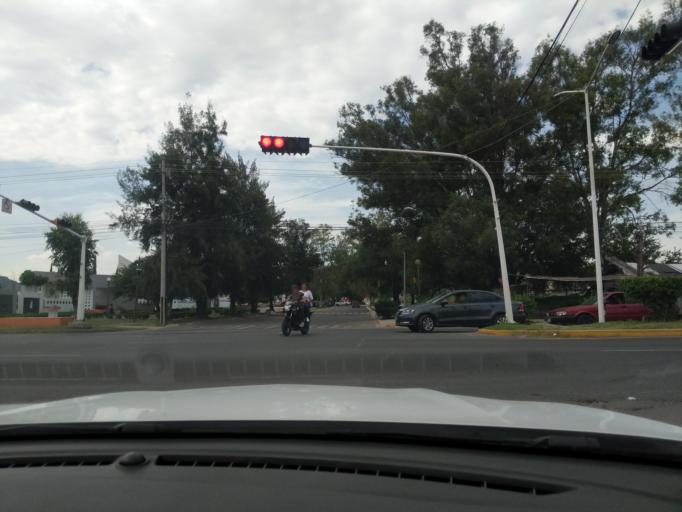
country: MX
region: Jalisco
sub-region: El Salto
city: Galaxia Bonito Jalisco
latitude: 20.5125
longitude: -103.1908
